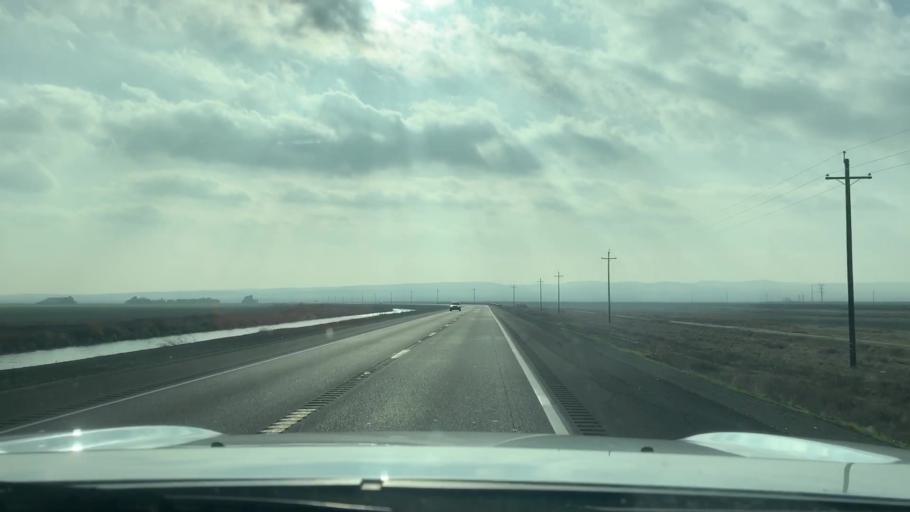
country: US
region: California
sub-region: Kings County
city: Kettleman City
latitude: 36.0623
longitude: -119.9376
